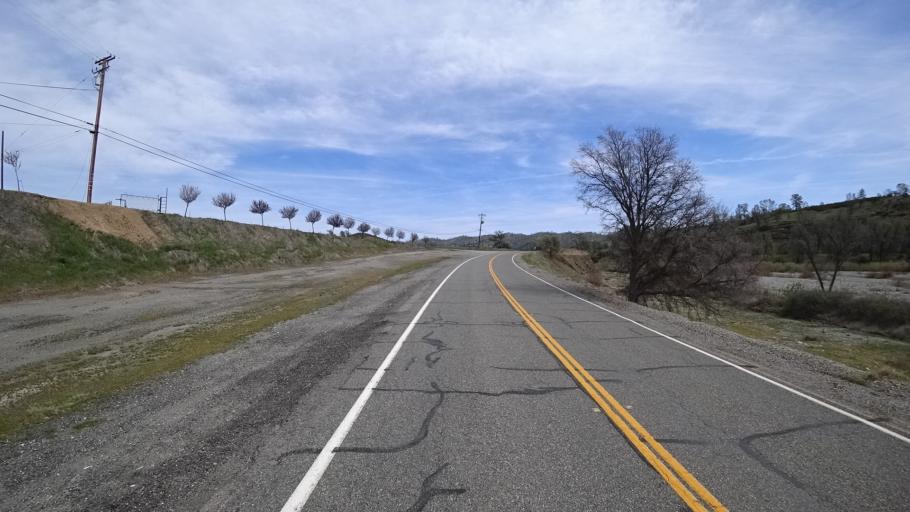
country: US
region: California
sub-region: Glenn County
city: Willows
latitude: 39.6094
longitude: -122.5337
